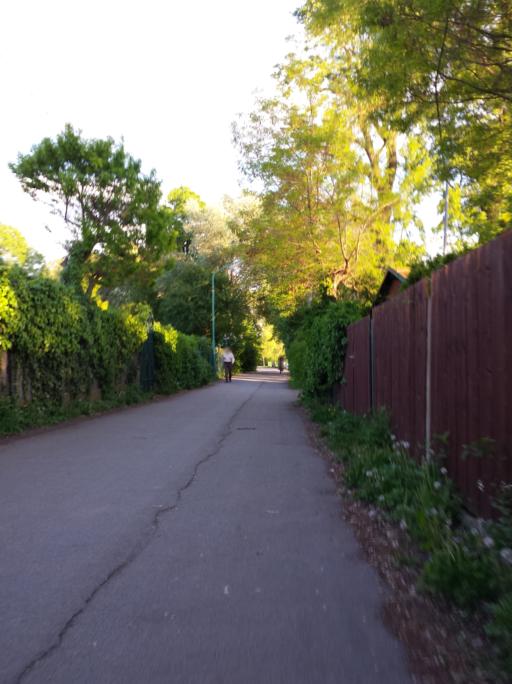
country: AT
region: Vienna
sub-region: Wien Stadt
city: Vienna
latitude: 48.2338
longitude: 16.4327
